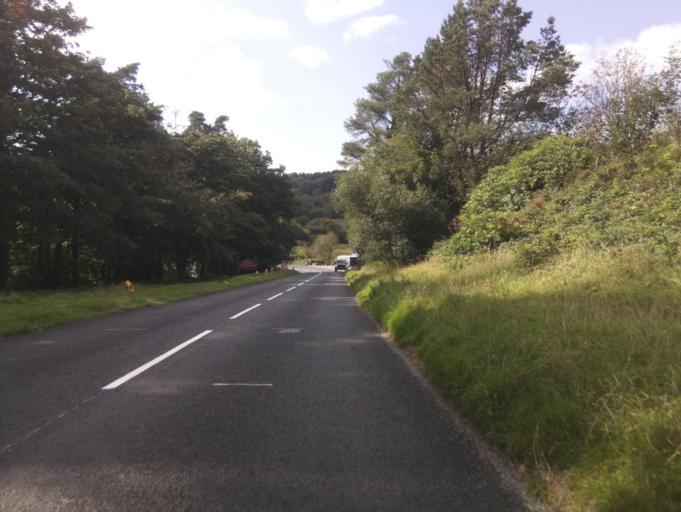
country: GB
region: England
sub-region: Devon
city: Yelverton
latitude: 50.5580
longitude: -3.9640
